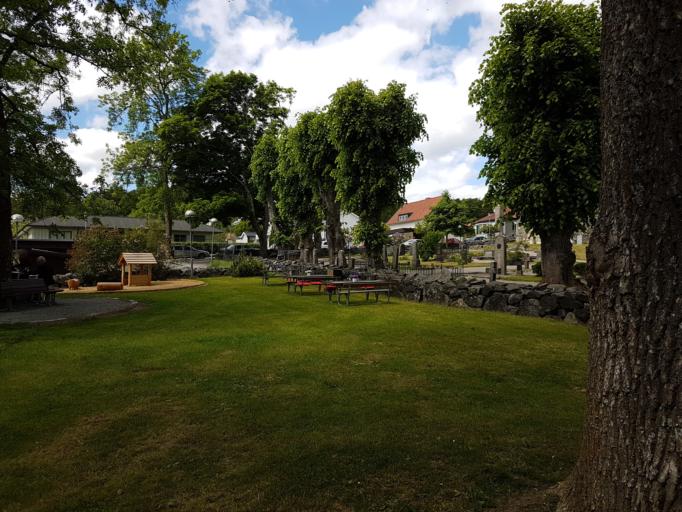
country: SE
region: Stockholm
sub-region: Sigtuna Kommun
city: Sigtuna
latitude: 59.6178
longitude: 17.7219
